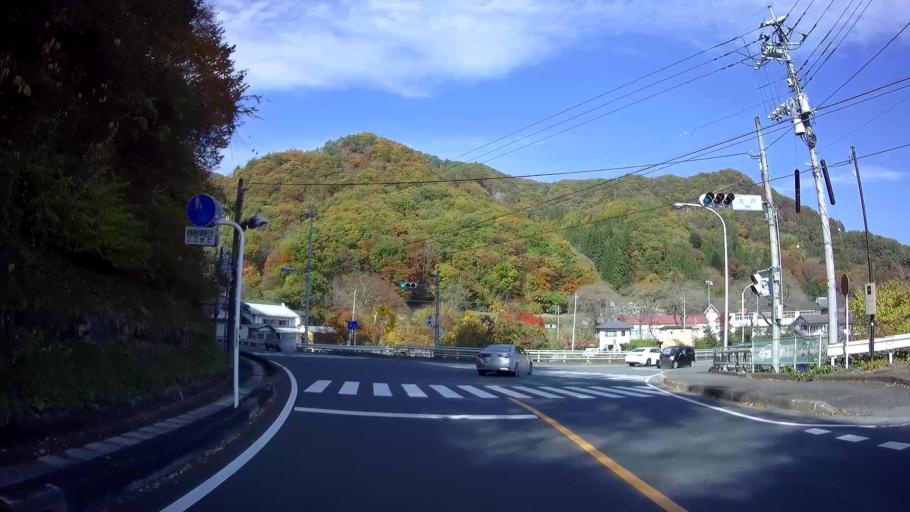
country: JP
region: Gunma
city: Nakanojomachi
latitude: 36.5129
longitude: 138.7746
